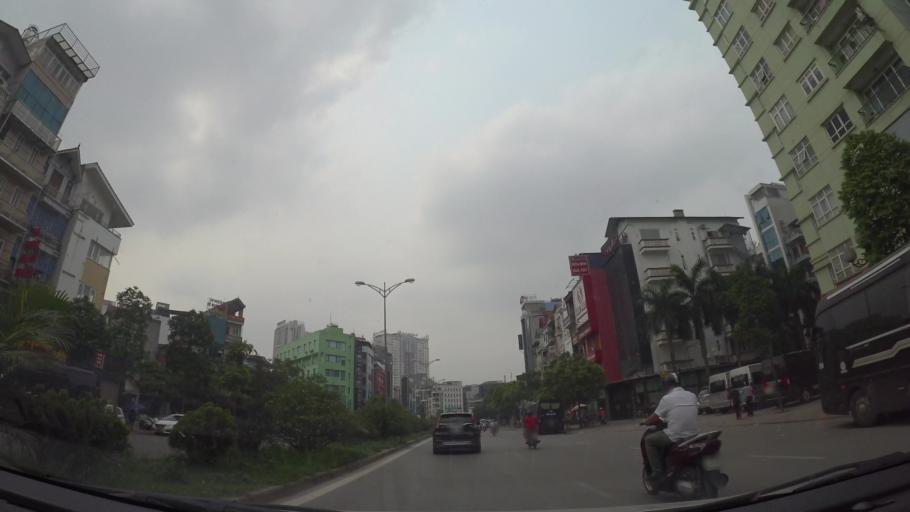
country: VN
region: Ha Noi
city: Cau Dien
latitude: 21.0309
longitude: 105.7747
